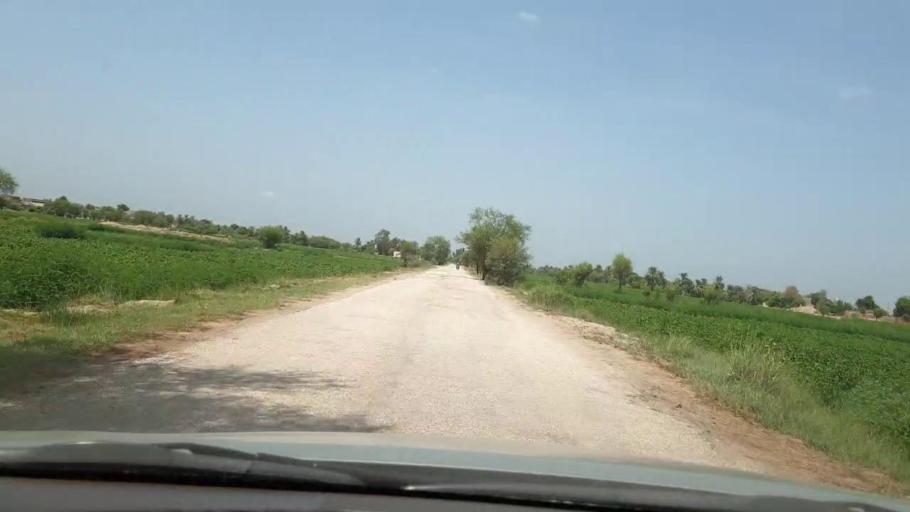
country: PK
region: Sindh
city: Pano Aqil
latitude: 27.7037
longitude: 69.2179
